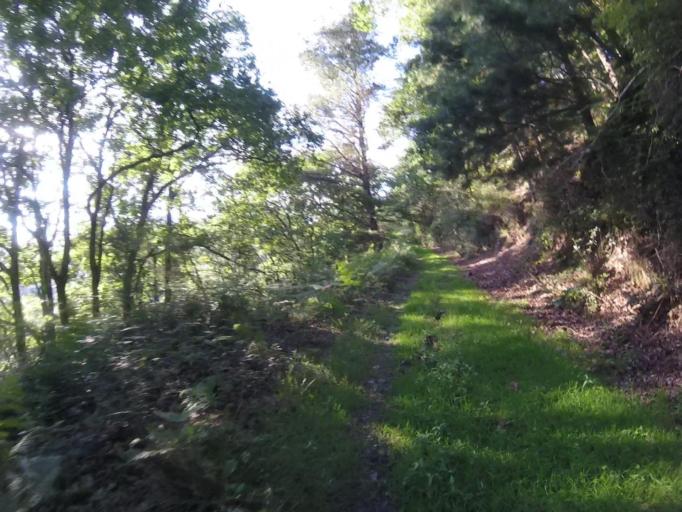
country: ES
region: Navarre
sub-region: Provincia de Navarra
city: Arano
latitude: 43.2265
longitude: -1.9067
